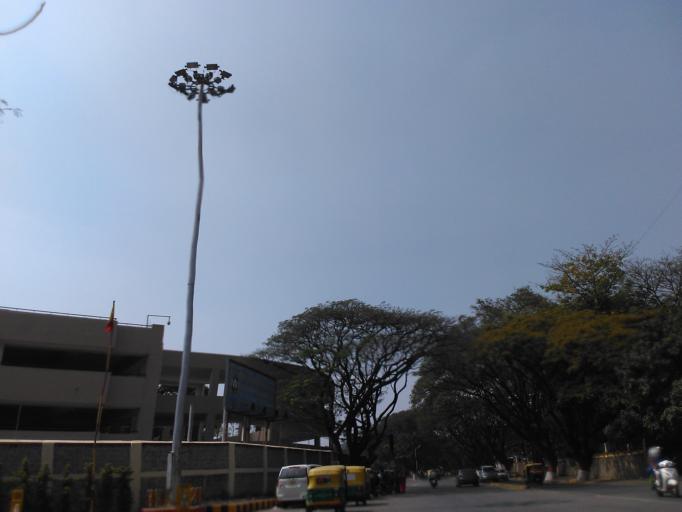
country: IN
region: Karnataka
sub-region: Bangalore Urban
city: Bangalore
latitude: 12.9810
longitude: 77.6571
